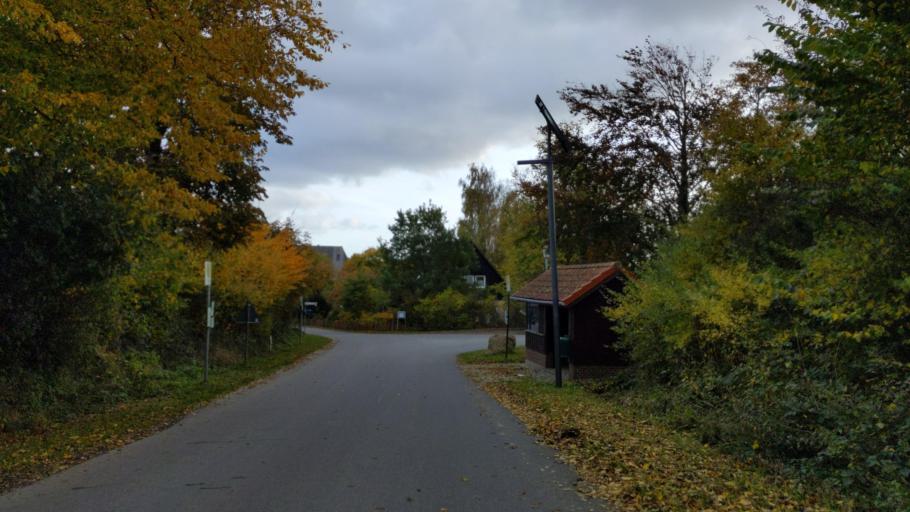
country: DE
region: Schleswig-Holstein
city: Kasseedorf
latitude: 54.1225
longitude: 10.7099
